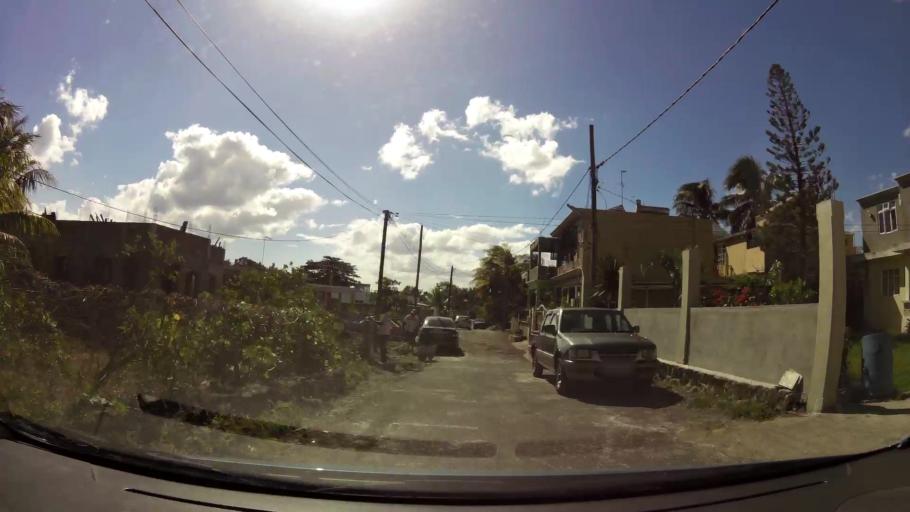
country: MU
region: Black River
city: Cascavelle
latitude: -20.2616
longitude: 57.4190
